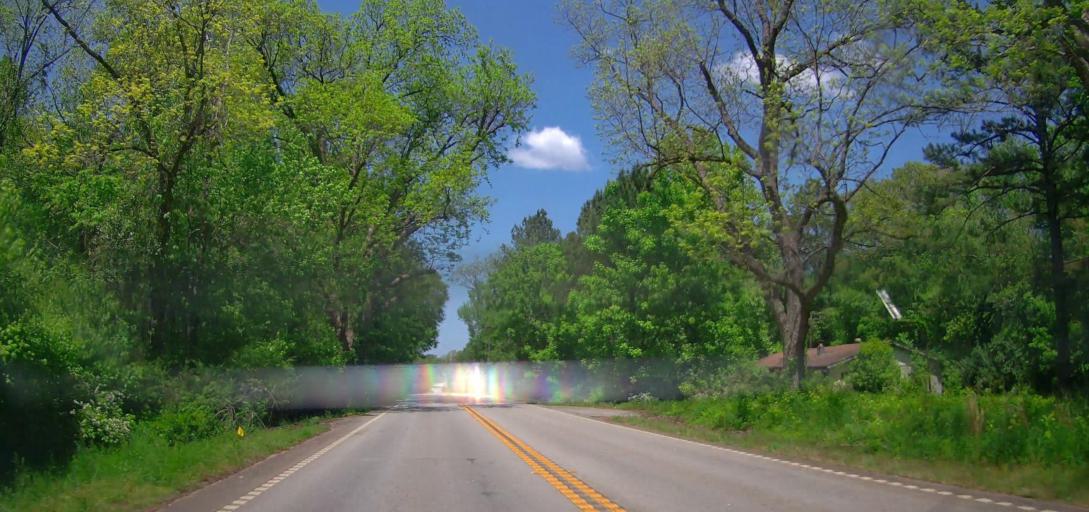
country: US
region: Georgia
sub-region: Jasper County
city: Monticello
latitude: 33.2918
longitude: -83.6786
